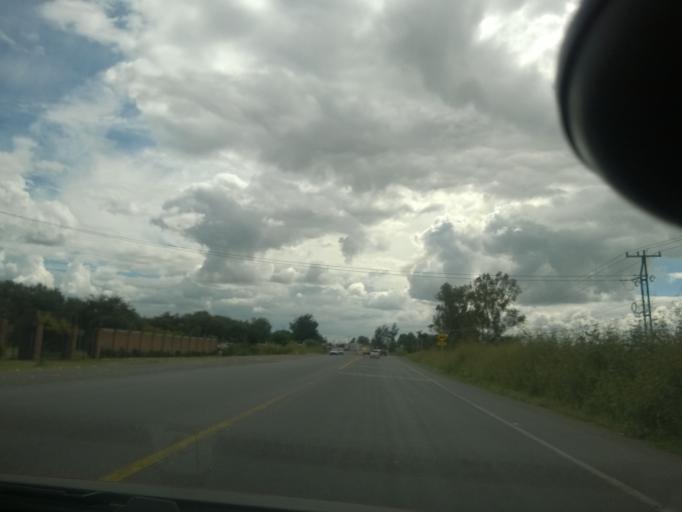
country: MX
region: Guanajuato
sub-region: Leon
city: El CERESO
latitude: 21.0002
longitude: -101.7030
